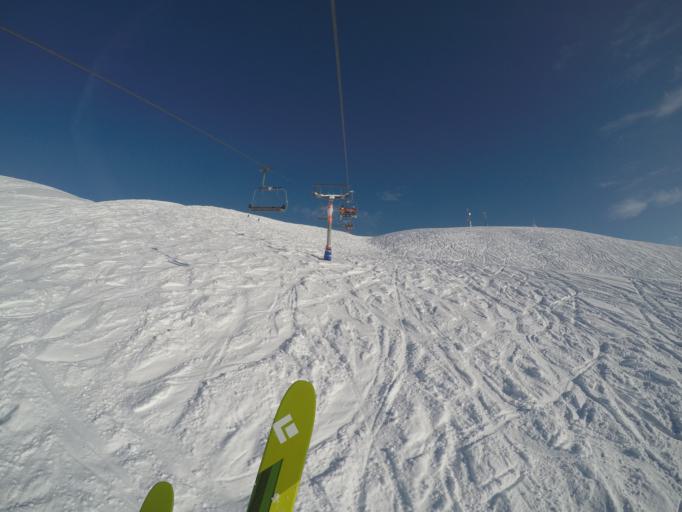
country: GE
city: Gudauri
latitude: 42.4864
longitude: 44.4970
